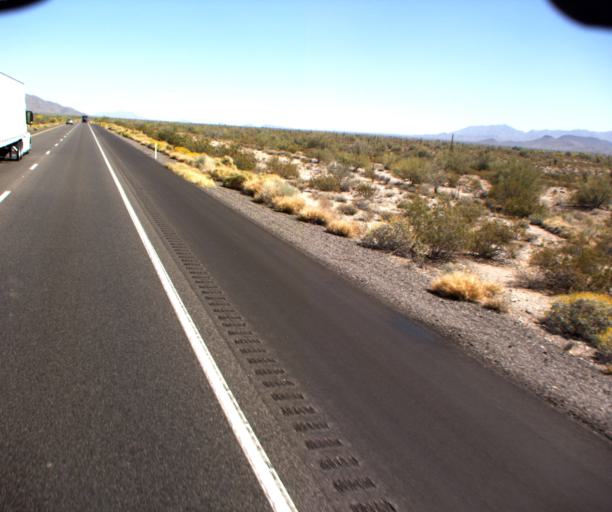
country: US
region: Arizona
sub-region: Maricopa County
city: Gila Bend
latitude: 32.8879
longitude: -112.4764
